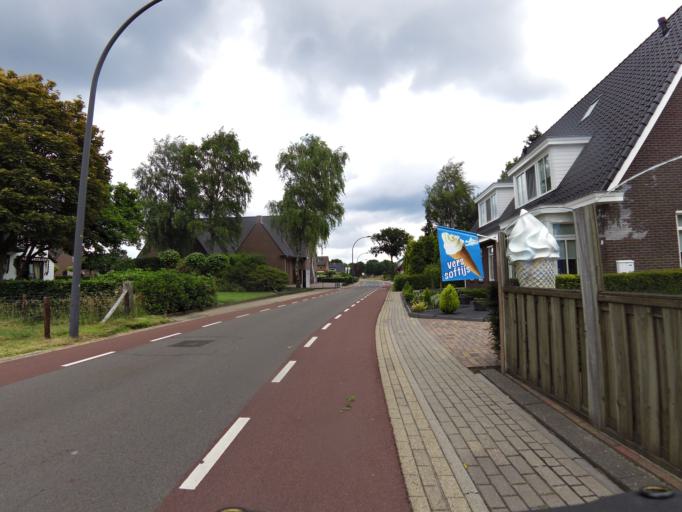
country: NL
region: Gelderland
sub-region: Gemeente Apeldoorn
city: Uddel
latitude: 52.2925
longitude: 5.7814
